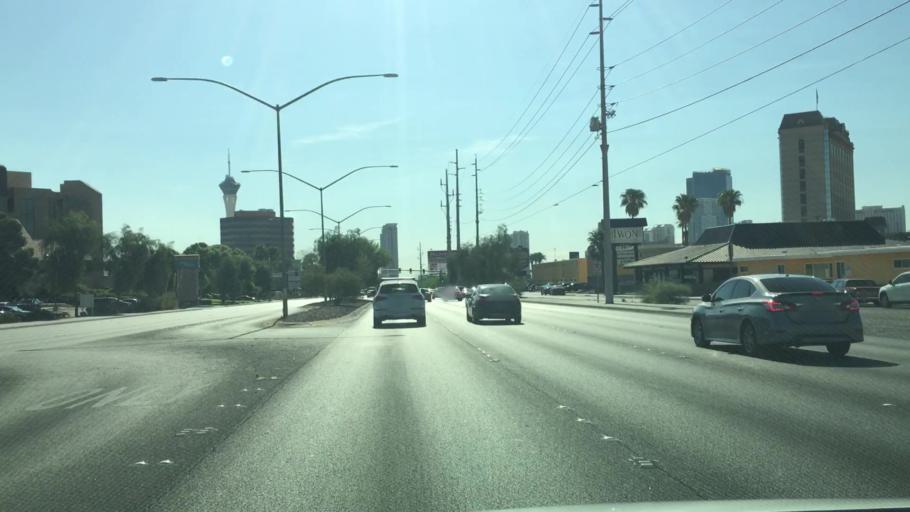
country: US
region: Nevada
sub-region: Clark County
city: Las Vegas
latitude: 36.1443
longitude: -115.1800
